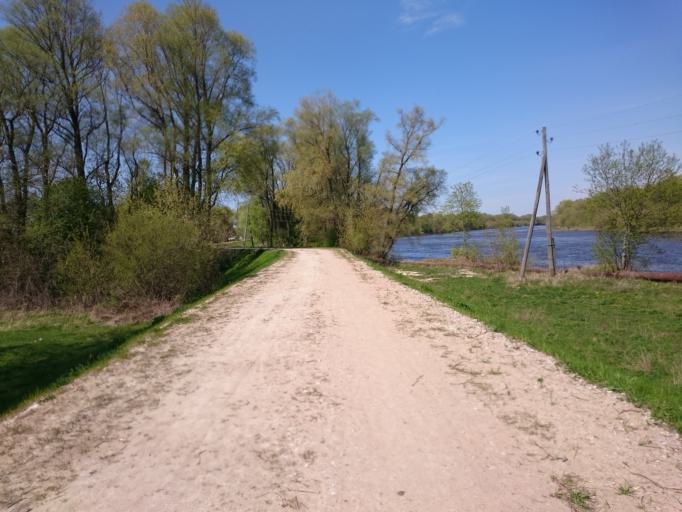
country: LV
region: Adazi
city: Adazi
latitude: 57.0837
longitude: 24.3260
